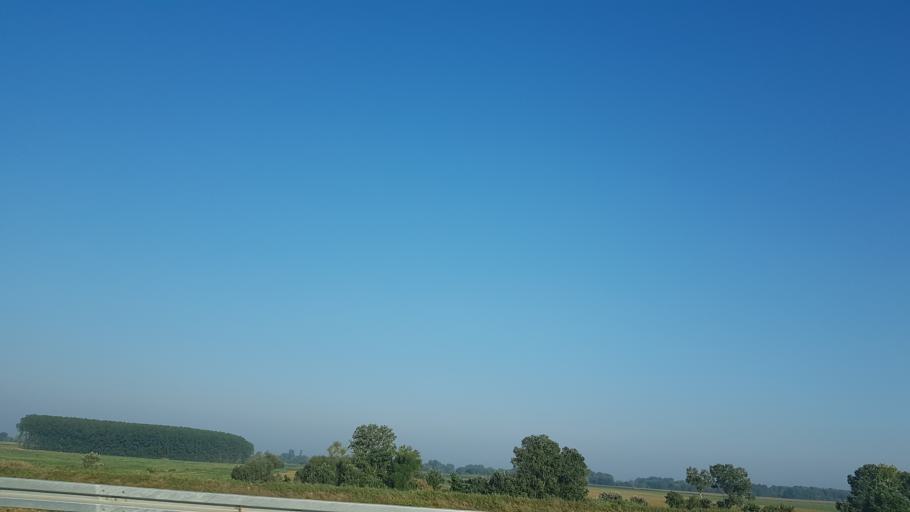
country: TR
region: Bursa
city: Karacabey
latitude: 40.1519
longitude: 28.3100
